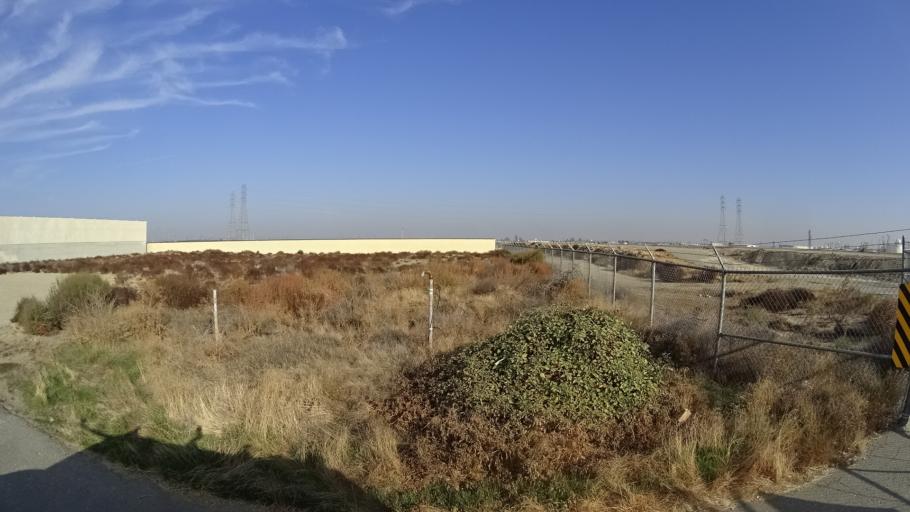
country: US
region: California
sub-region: Kern County
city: Greenacres
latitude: 35.3691
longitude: -119.0879
